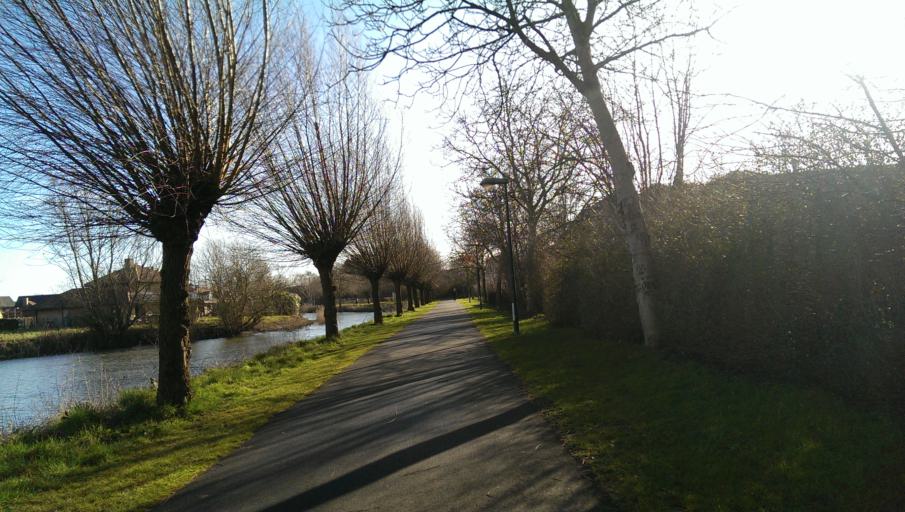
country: BE
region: Flanders
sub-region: Provincie West-Vlaanderen
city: Roeselare
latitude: 50.9542
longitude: 3.1077
